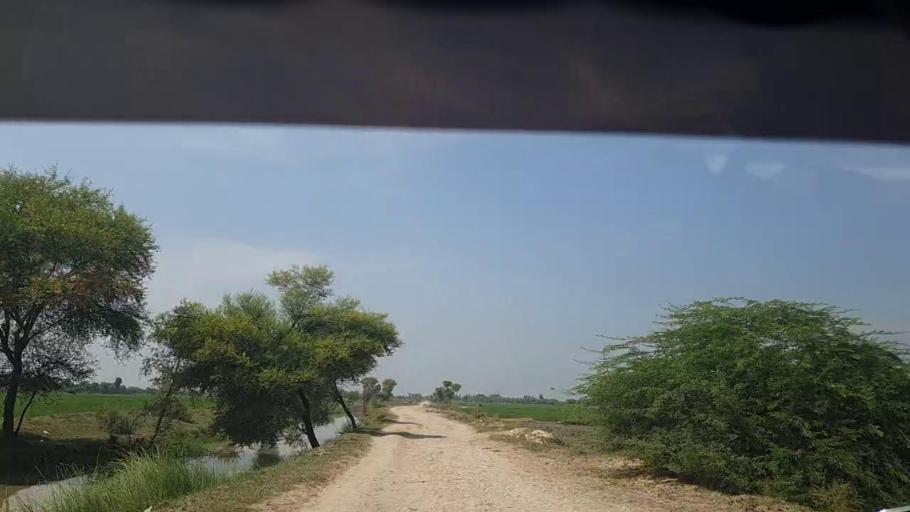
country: PK
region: Sindh
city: Thul
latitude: 28.1931
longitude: 68.7103
